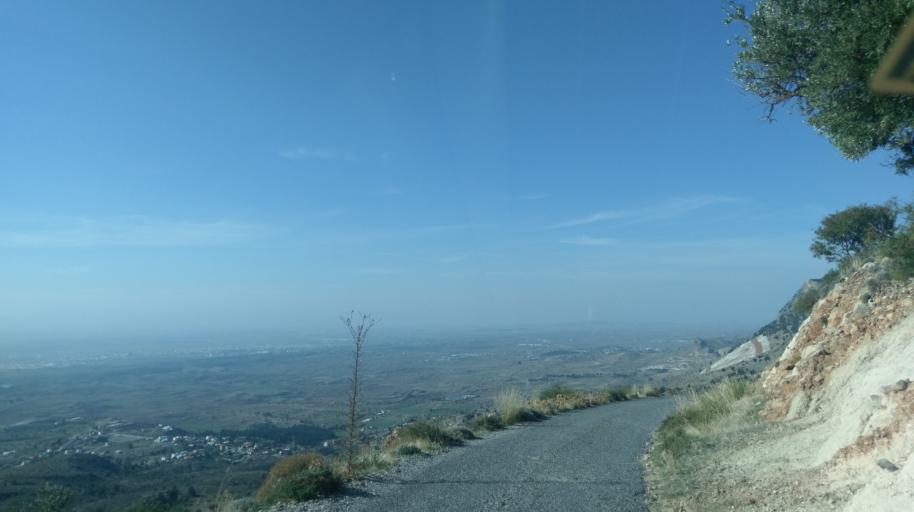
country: CY
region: Keryneia
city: Kyrenia
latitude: 35.2838
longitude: 33.3997
